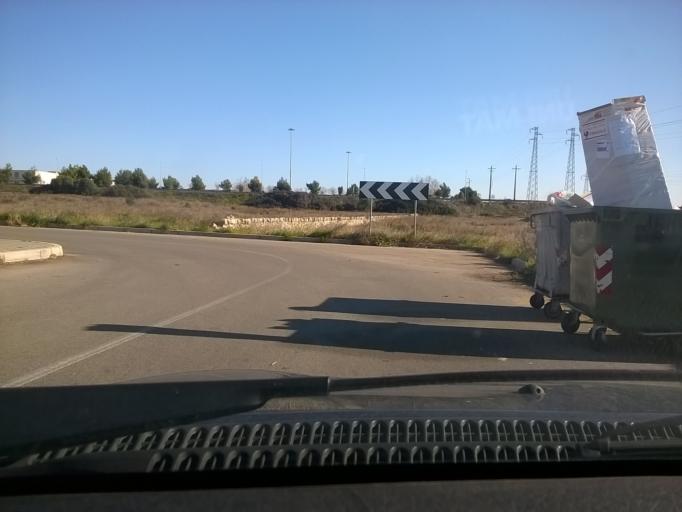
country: IT
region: Apulia
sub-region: Provincia di Taranto
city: Paolo VI
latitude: 40.5154
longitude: 17.2863
